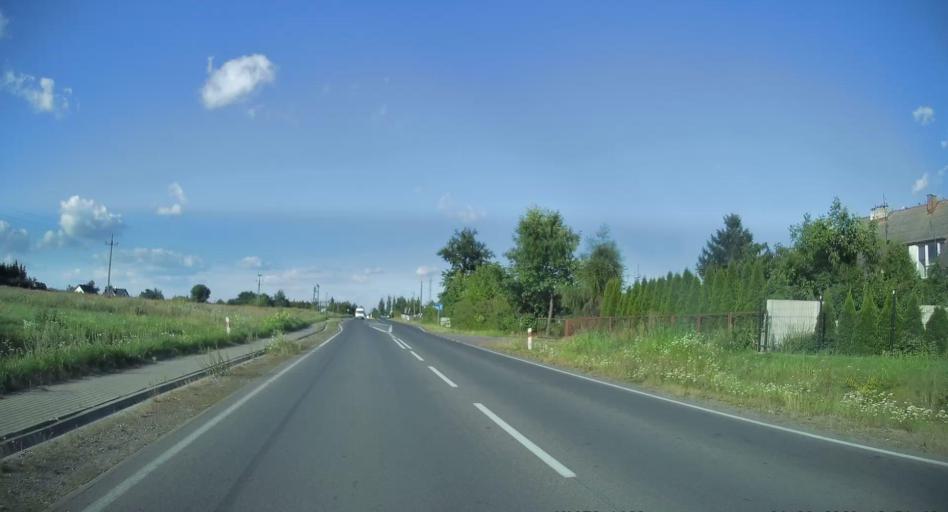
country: PL
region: Masovian Voivodeship
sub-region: Powiat grojecki
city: Grojec
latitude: 51.8520
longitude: 20.8432
